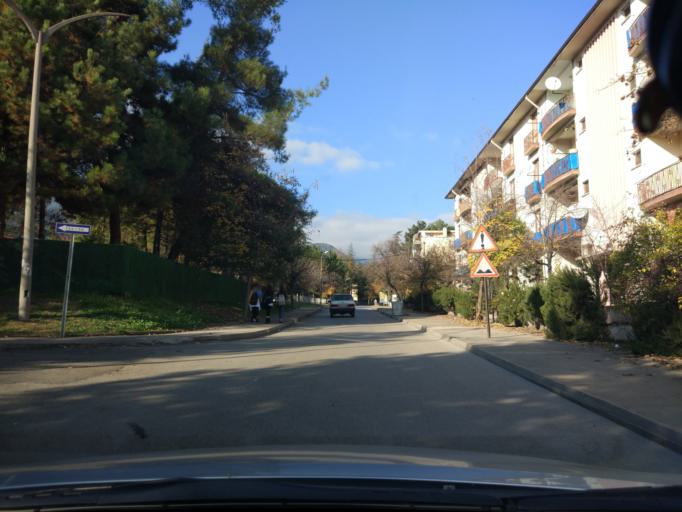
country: TR
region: Karabuk
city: Karabuk
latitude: 41.1989
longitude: 32.6225
